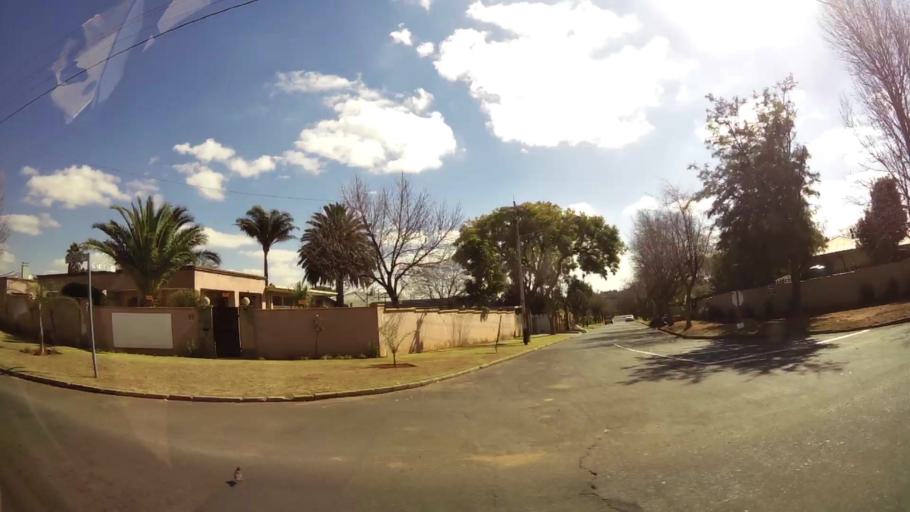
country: ZA
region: Gauteng
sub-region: West Rand District Municipality
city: Krugersdorp
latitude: -26.0918
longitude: 27.7855
